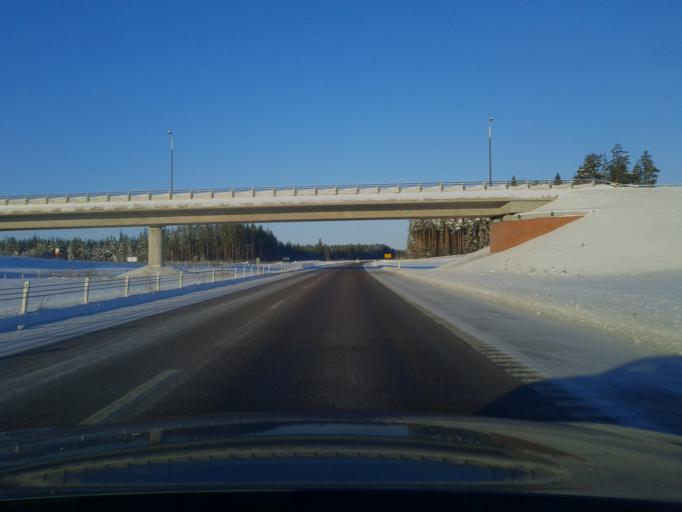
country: SE
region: Uppsala
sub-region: Alvkarleby Kommun
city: AElvkarleby
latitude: 60.4384
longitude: 17.4217
